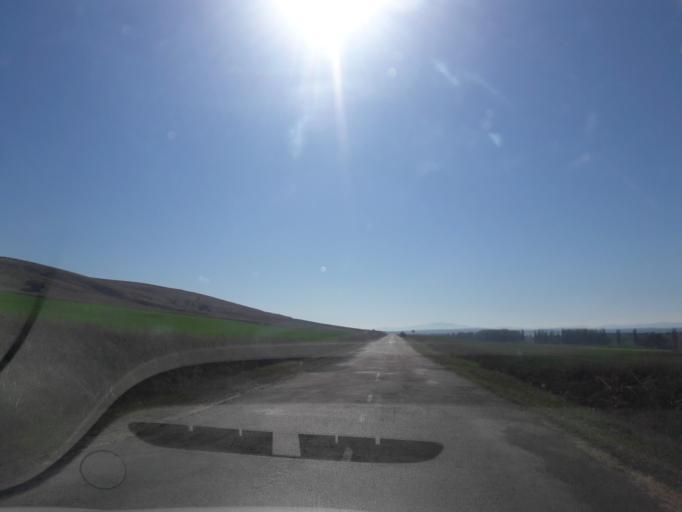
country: ES
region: Castille and Leon
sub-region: Provincia de Salamanca
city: Mancera de Abajo
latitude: 40.8316
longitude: -5.1888
